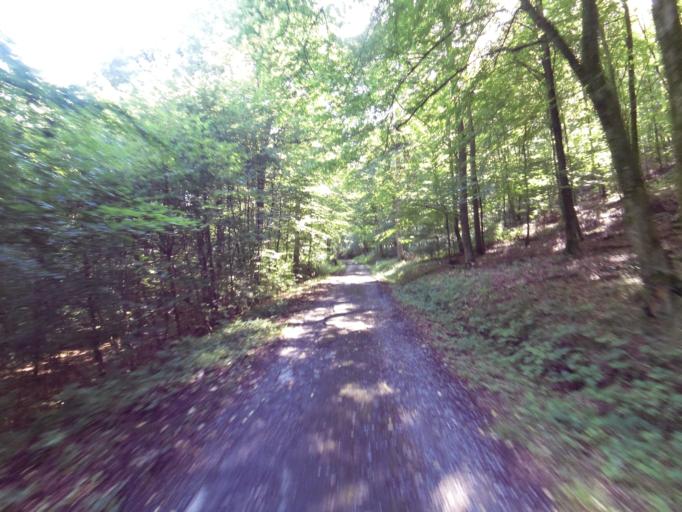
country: BE
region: Wallonia
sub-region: Province du Luxembourg
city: Nassogne
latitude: 50.0914
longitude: 5.3429
